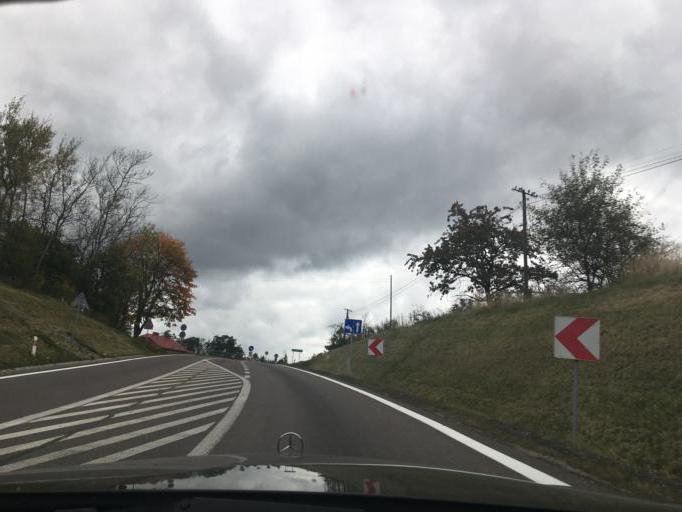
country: PL
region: Subcarpathian Voivodeship
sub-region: Powiat brzozowski
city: Jablonica Polska
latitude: 49.7178
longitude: 21.9008
